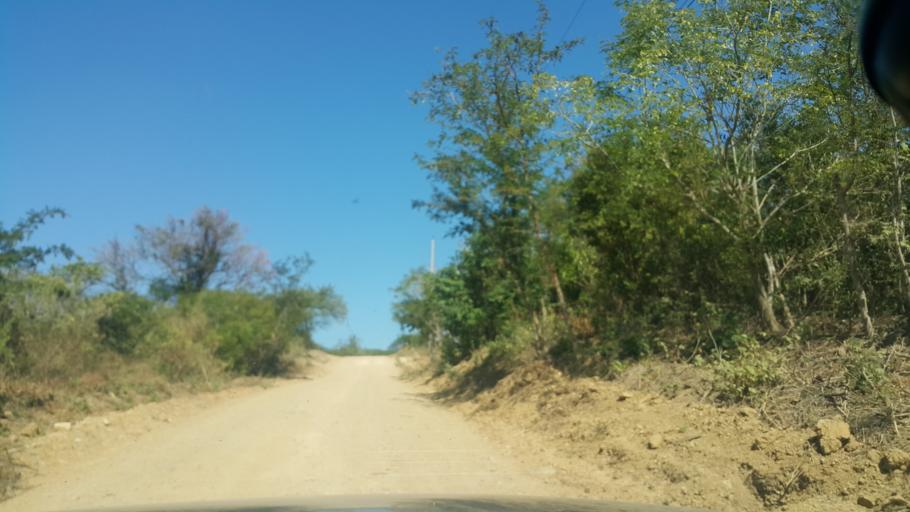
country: NI
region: Rivas
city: San Juan del Sur
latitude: 11.2808
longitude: -85.8845
